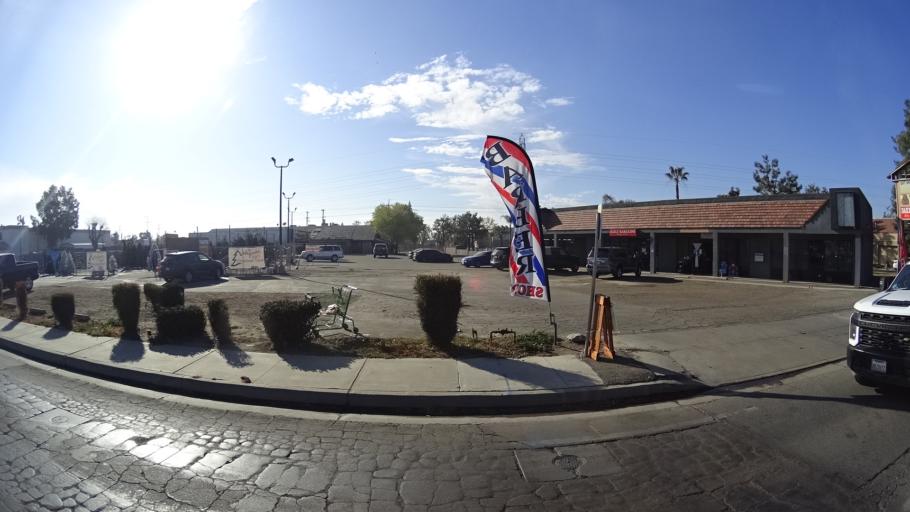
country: US
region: California
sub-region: Kern County
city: Bakersfield
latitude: 35.3177
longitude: -119.0543
